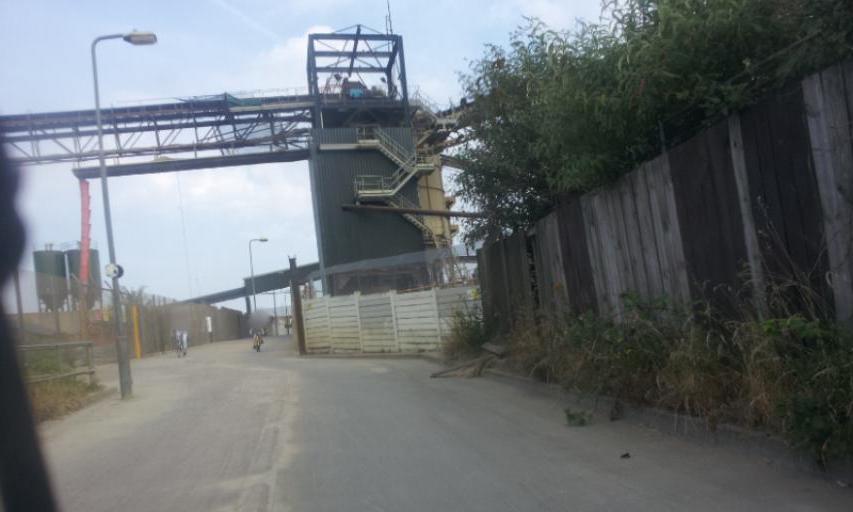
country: GB
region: England
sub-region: Greater London
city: Blackheath
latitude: 51.4939
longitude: 0.0217
